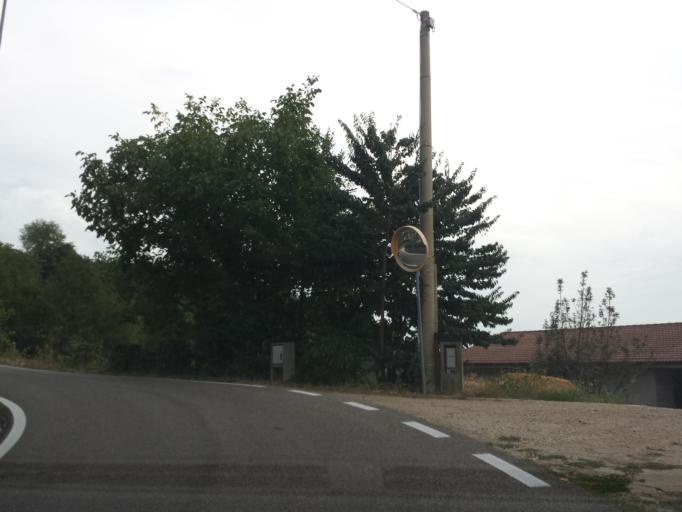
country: IT
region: Veneto
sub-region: Provincia di Vicenza
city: Valdagno
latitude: 45.6422
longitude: 11.3198
